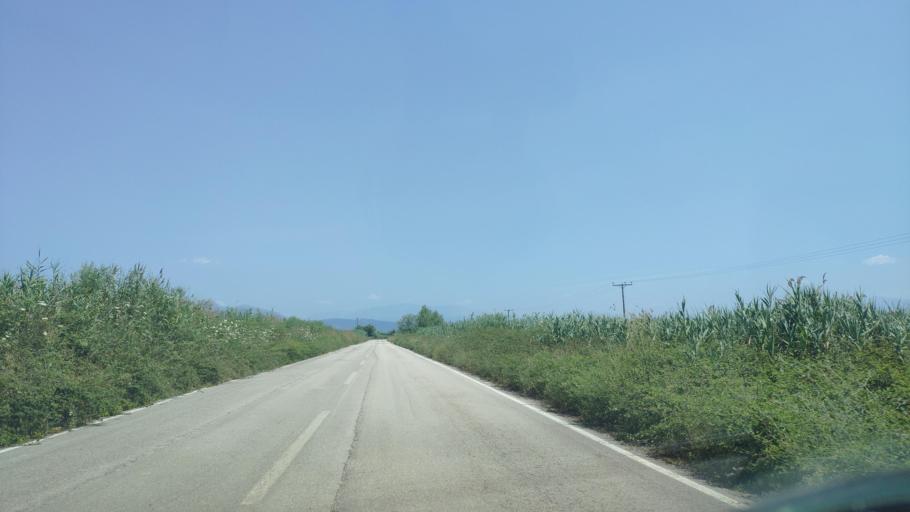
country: GR
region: Epirus
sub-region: Nomos Artas
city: Aneza
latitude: 39.0715
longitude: 20.8802
